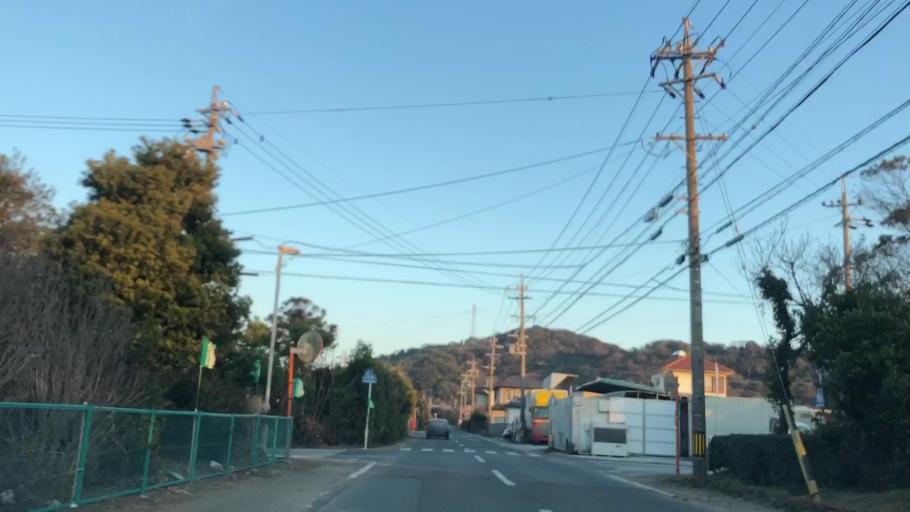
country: JP
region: Aichi
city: Toyohama
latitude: 34.6060
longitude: 137.0541
